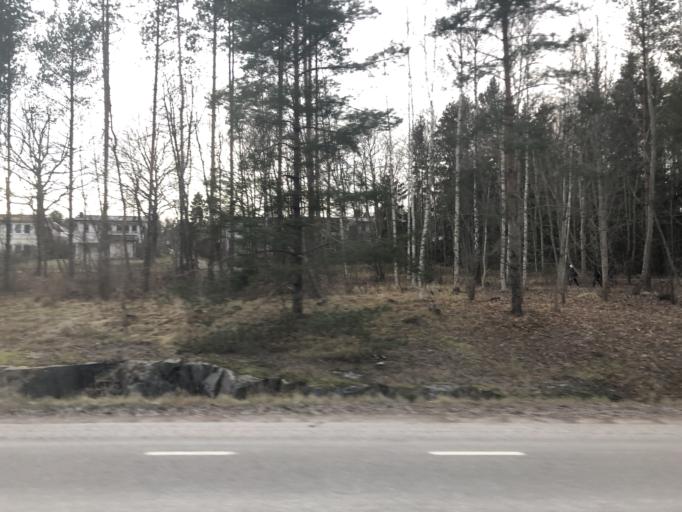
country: SE
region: Stockholm
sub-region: Jarfalla Kommun
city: Jakobsberg
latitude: 59.4119
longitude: 17.7967
